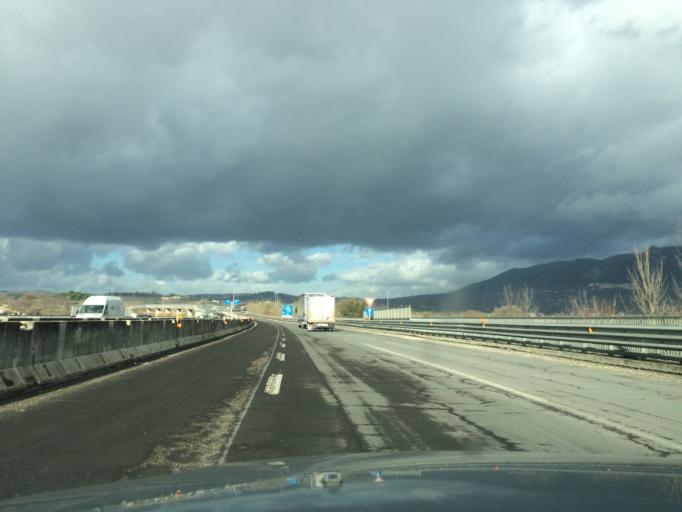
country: IT
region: Umbria
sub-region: Provincia di Terni
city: Terni
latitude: 42.5631
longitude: 12.5807
